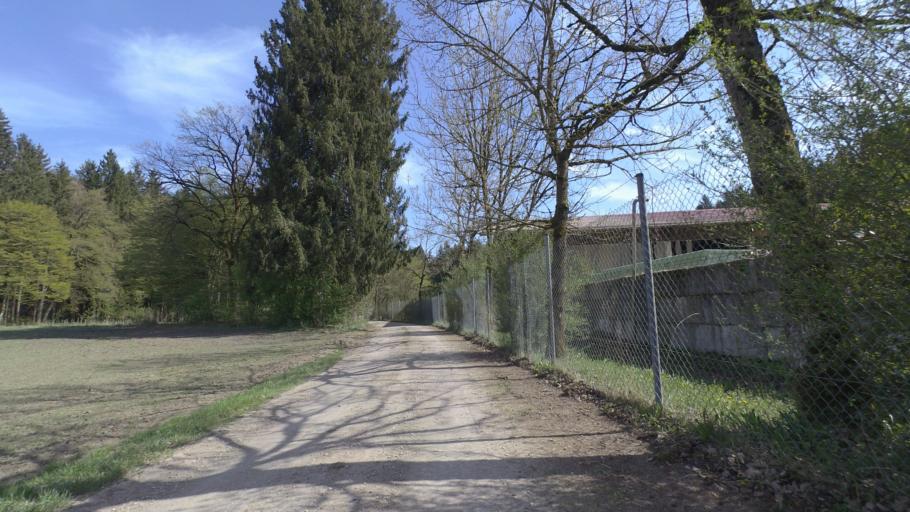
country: DE
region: Bavaria
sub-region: Upper Bavaria
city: Nussdorf
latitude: 47.9181
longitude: 12.5771
